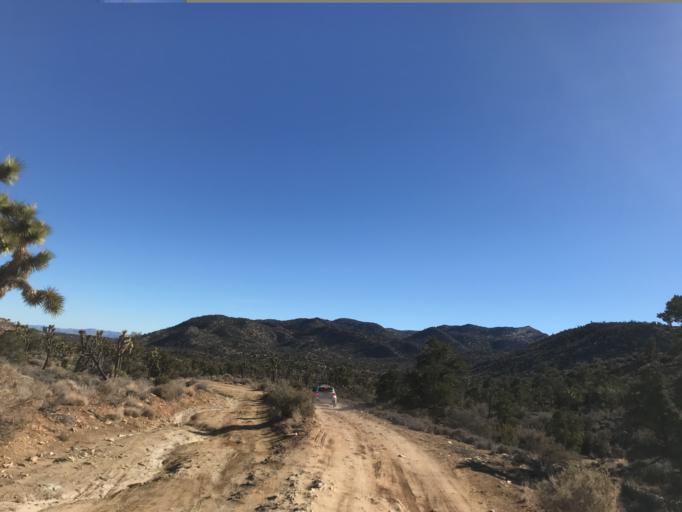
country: US
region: California
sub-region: San Bernardino County
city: Morongo Valley
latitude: 34.2328
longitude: -116.6439
